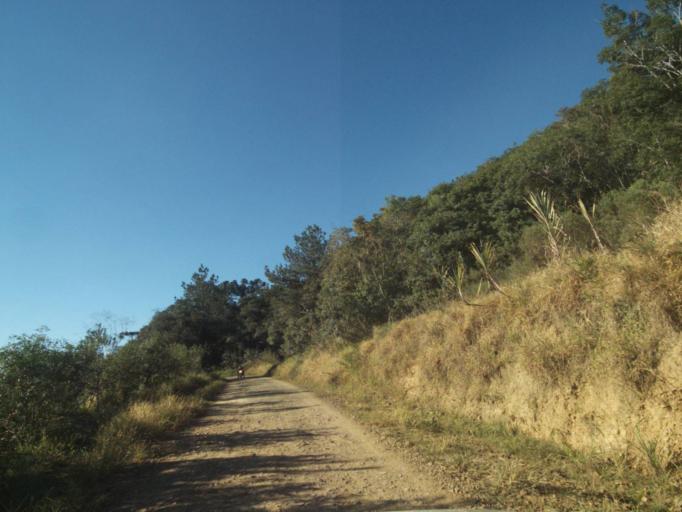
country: BR
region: Parana
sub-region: Tibagi
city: Tibagi
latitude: -24.5500
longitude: -50.5167
